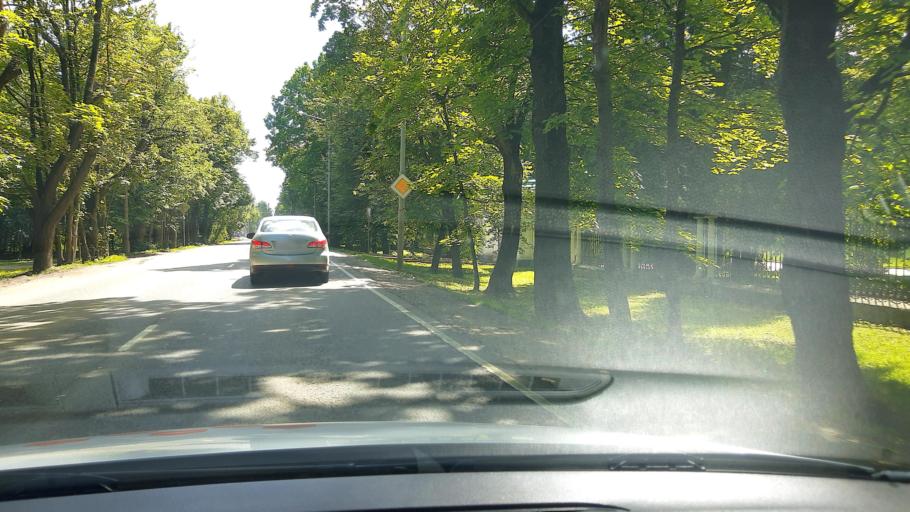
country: RU
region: Moskovskaya
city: Filimonki
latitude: 55.5747
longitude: 37.3552
